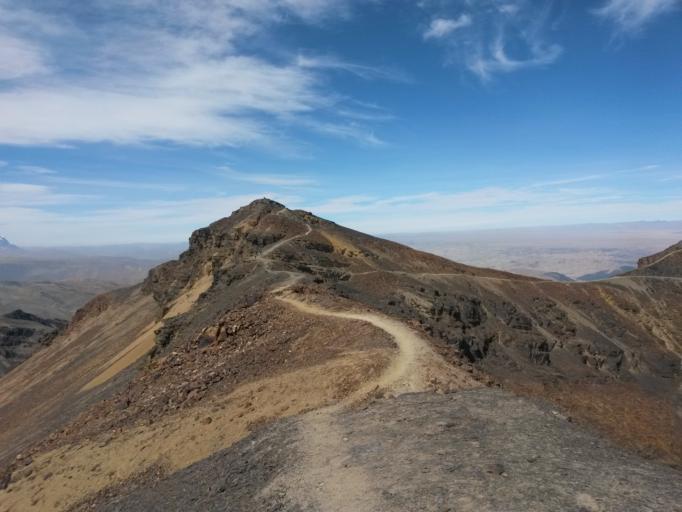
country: BO
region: La Paz
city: La Paz
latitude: -16.3475
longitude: -68.1279
